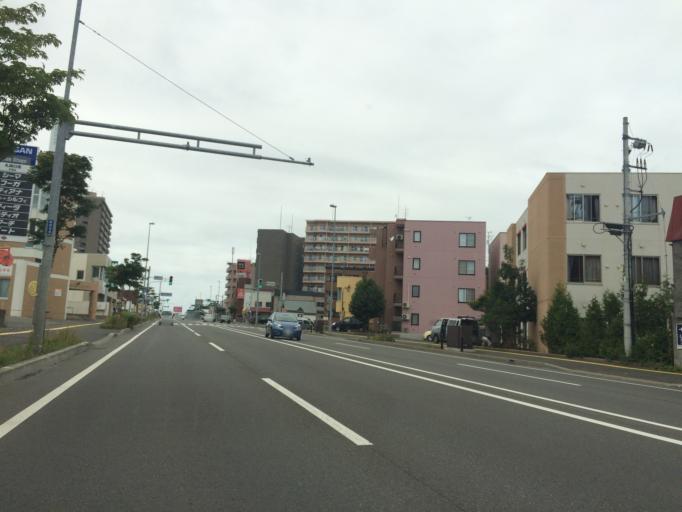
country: JP
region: Hokkaido
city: Sapporo
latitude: 43.1175
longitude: 141.2410
